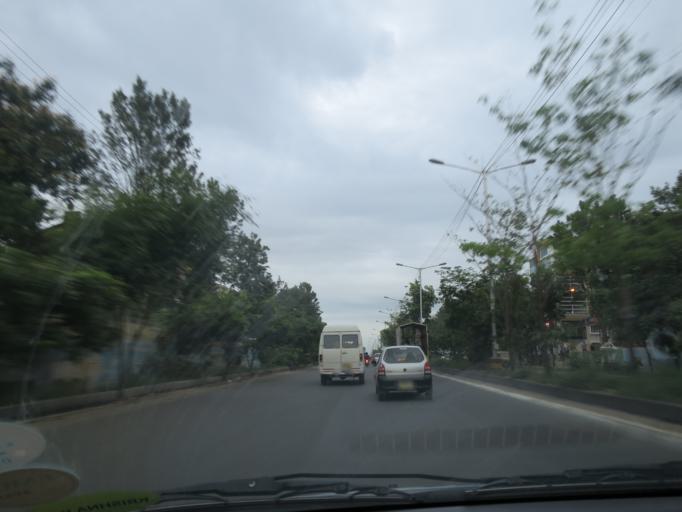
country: IN
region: Karnataka
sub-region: Bangalore Urban
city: Bangalore
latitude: 12.9705
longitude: 77.7002
